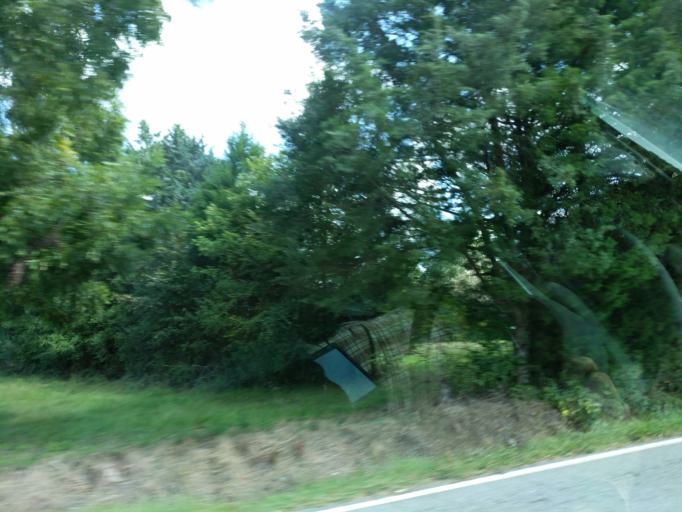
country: US
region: South Carolina
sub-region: Spartanburg County
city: Woodruff
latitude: 34.7200
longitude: -82.0455
